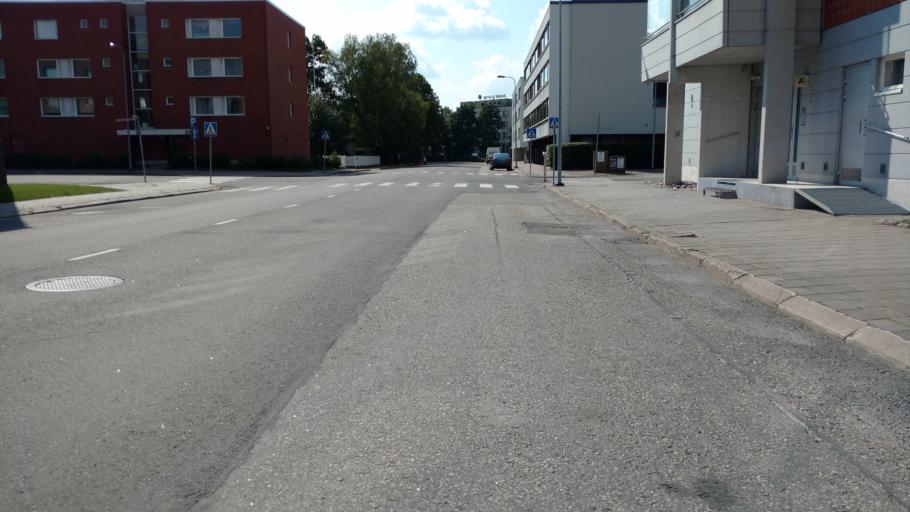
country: FI
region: Varsinais-Suomi
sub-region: Salo
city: Salo
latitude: 60.3877
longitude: 23.1321
